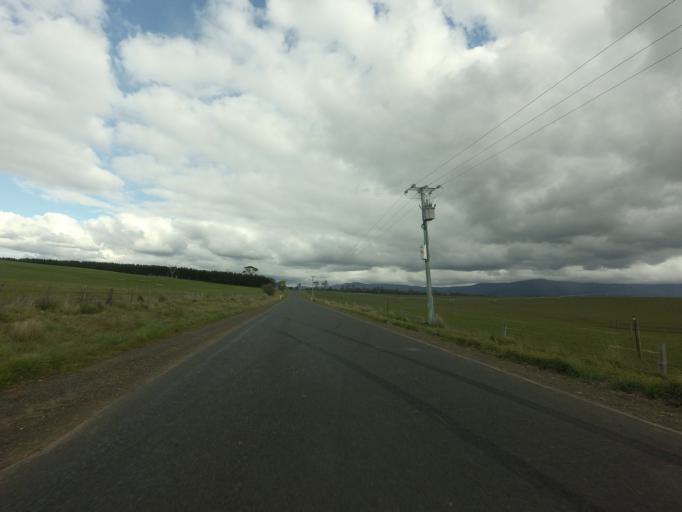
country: AU
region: Tasmania
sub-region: Northern Midlands
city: Longford
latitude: -41.7566
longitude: 147.0826
